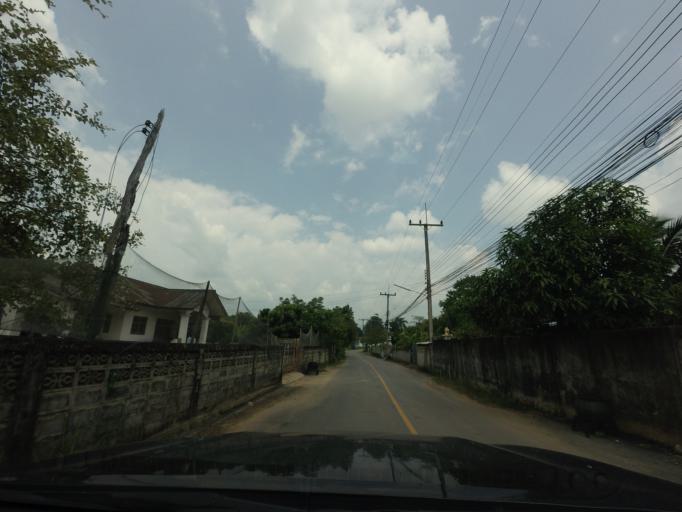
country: TH
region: Nan
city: Pua
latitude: 19.1666
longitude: 100.9263
